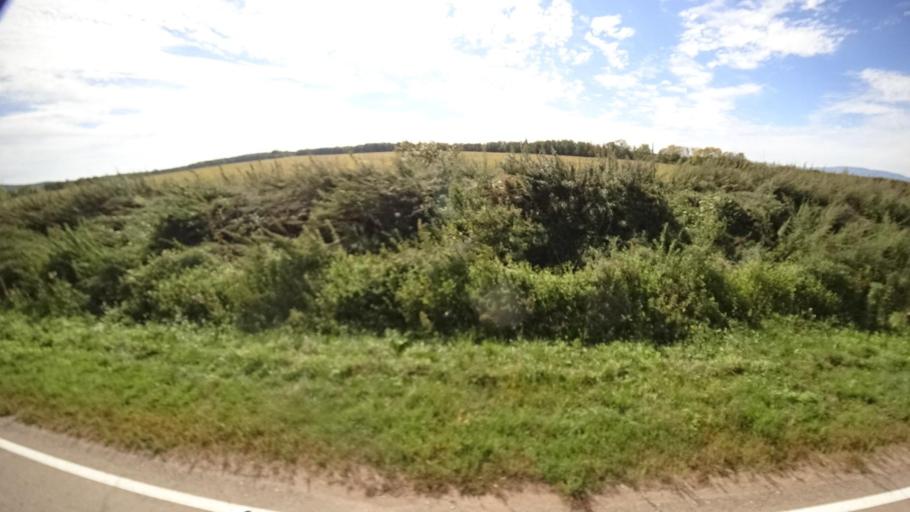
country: RU
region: Primorskiy
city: Yakovlevka
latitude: 44.4238
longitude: 133.5767
